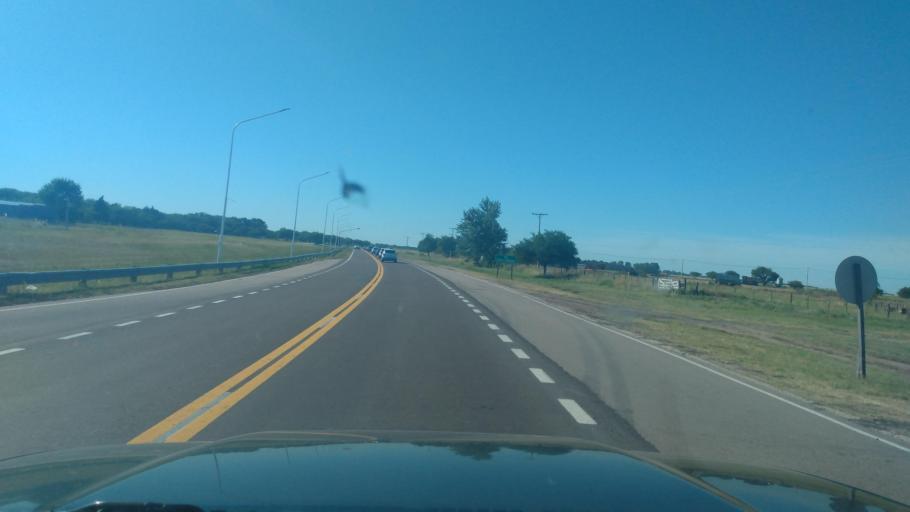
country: AR
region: La Pampa
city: Doblas
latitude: -37.0362
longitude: -64.2884
